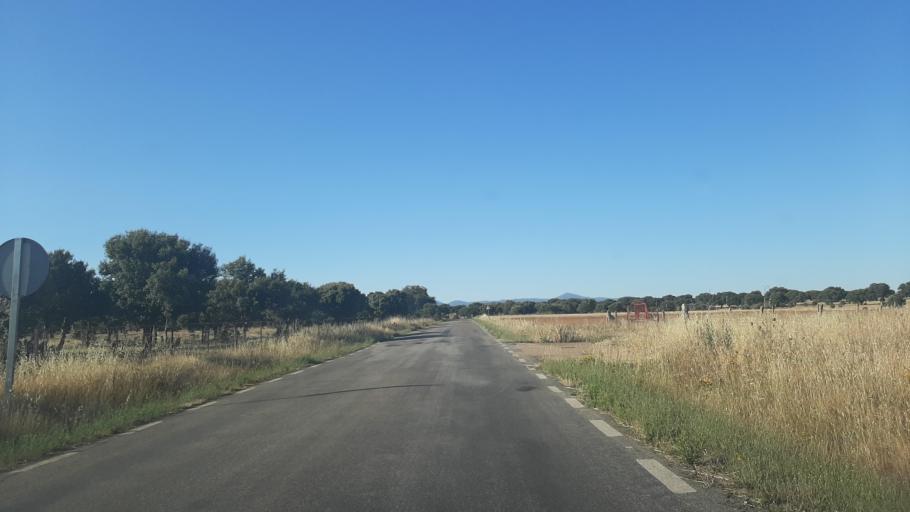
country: ES
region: Castille and Leon
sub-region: Provincia de Salamanca
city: Cabrillas
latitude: 40.7331
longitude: -6.1775
